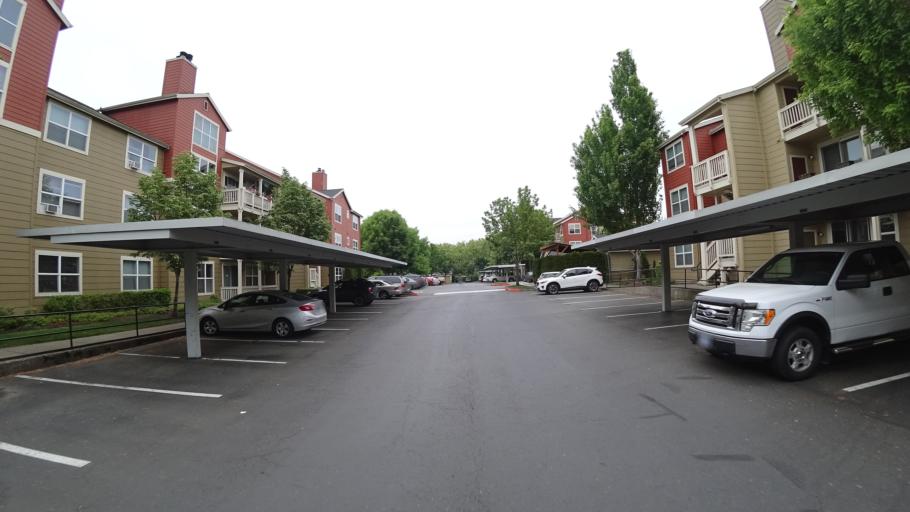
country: US
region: Oregon
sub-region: Washington County
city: Rockcreek
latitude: 45.5408
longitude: -122.8778
